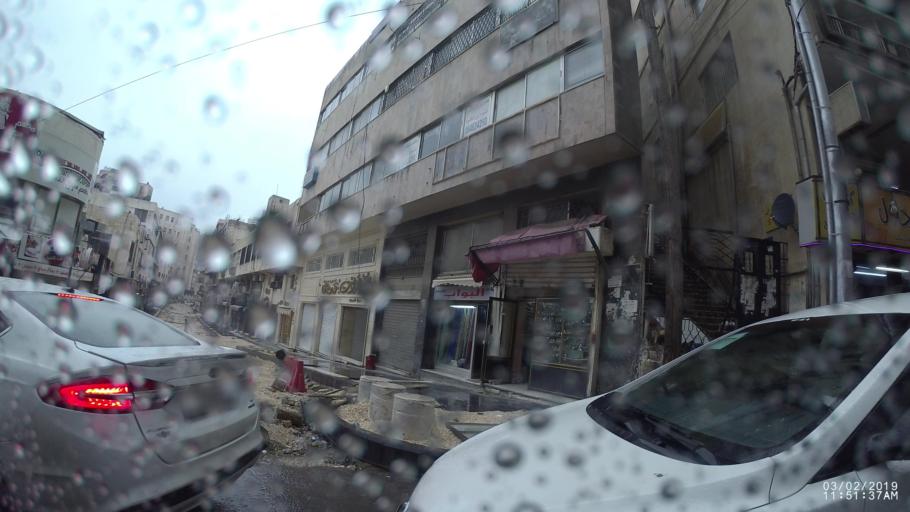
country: JO
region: Amman
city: Amman
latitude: 31.9515
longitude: 35.9347
